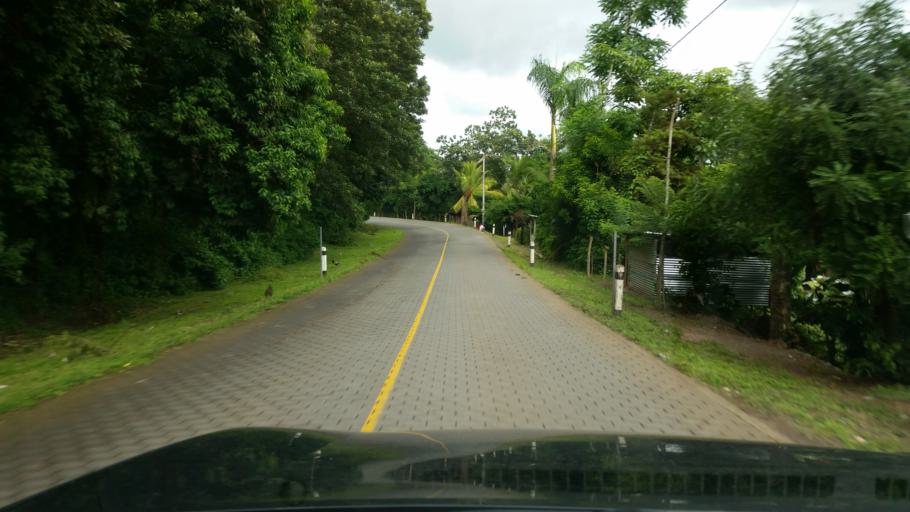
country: NI
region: Jinotega
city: Jinotega
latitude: 13.2059
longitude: -85.7198
